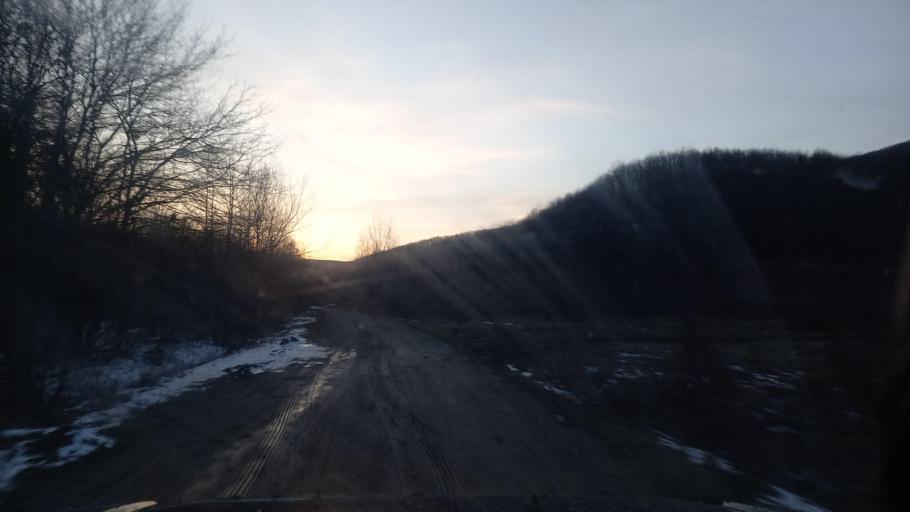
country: RU
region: Krasnodarskiy
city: Smolenskaya
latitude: 44.6238
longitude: 38.8222
